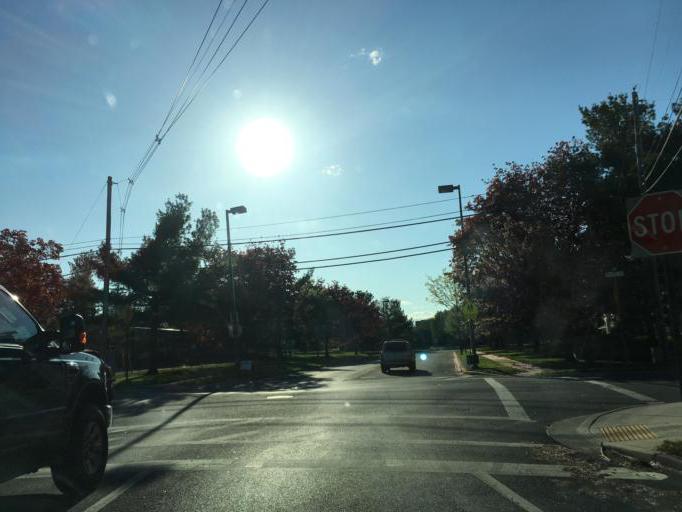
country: US
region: Maryland
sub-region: Frederick County
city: Frederick
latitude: 39.4259
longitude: -77.4102
